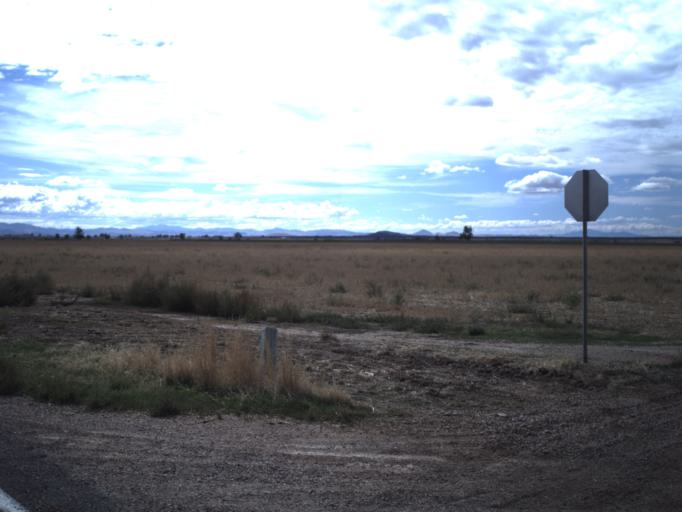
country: US
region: Utah
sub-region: Millard County
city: Fillmore
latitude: 39.0522
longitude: -112.4098
